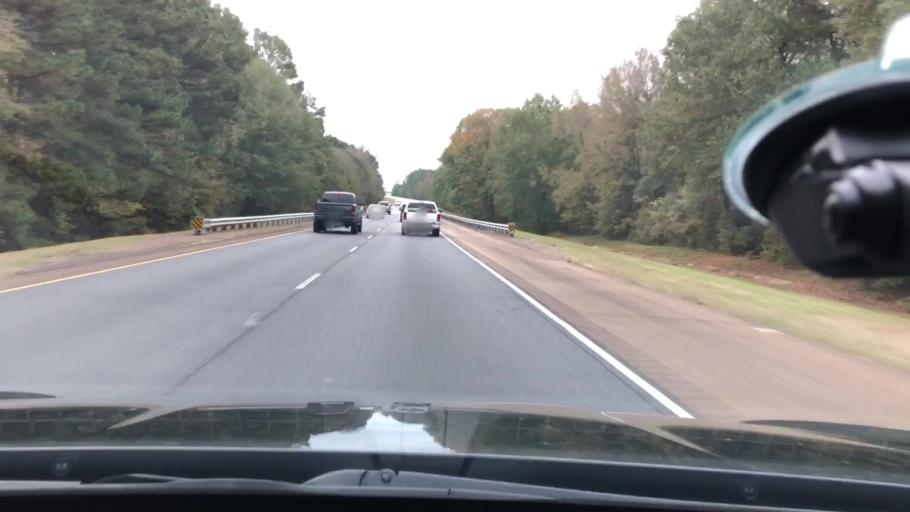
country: US
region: Arkansas
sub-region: Nevada County
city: Prescott
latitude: 33.8720
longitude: -93.3390
